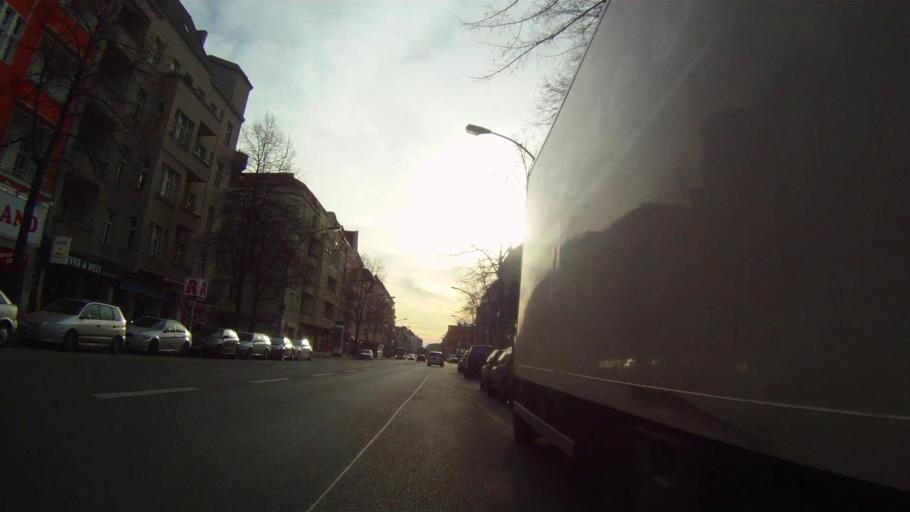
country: DE
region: Berlin
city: Britz
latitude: 52.4696
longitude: 13.4301
